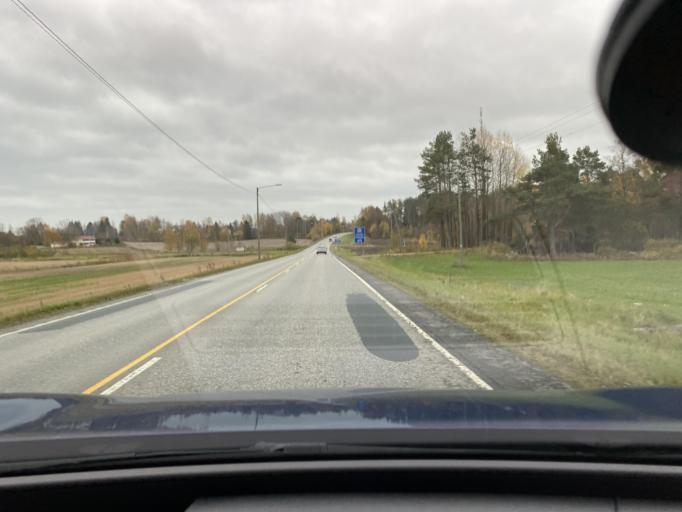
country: FI
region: Varsinais-Suomi
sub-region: Vakka-Suomi
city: Pyhaeranta
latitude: 60.9900
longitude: 21.5827
